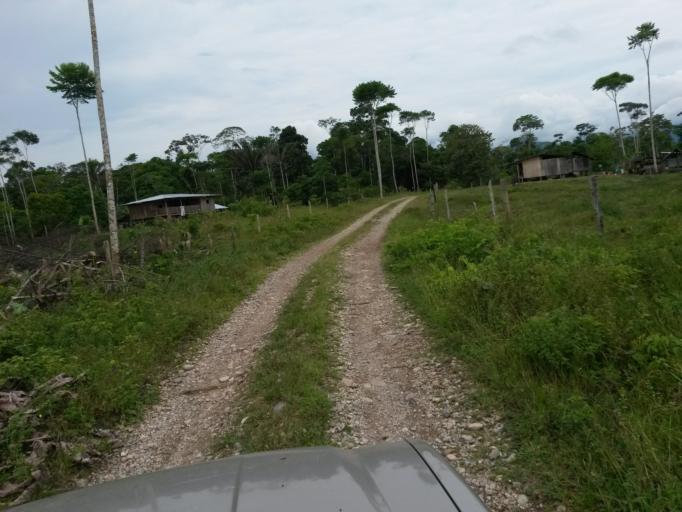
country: CO
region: Putumayo
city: Puerto Guzman
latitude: 1.0230
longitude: -76.3754
